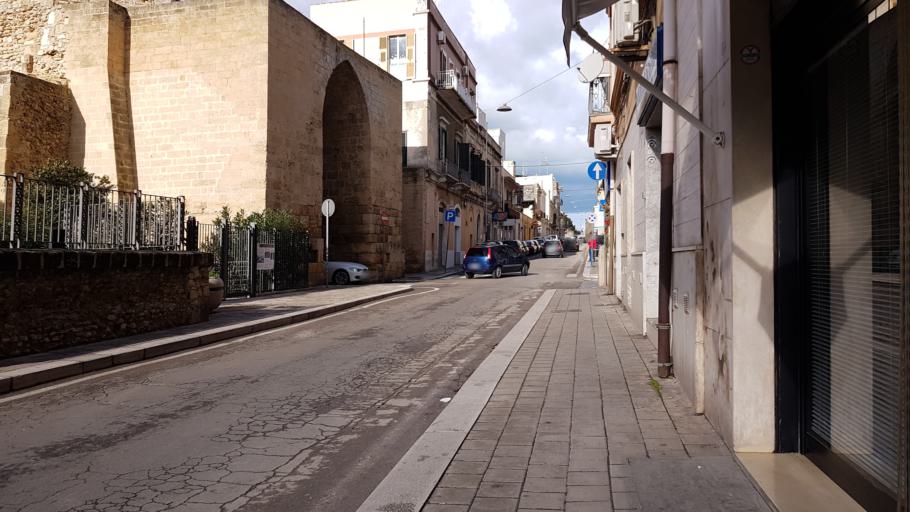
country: IT
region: Apulia
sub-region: Provincia di Brindisi
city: Brindisi
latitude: 40.6363
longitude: 17.9395
